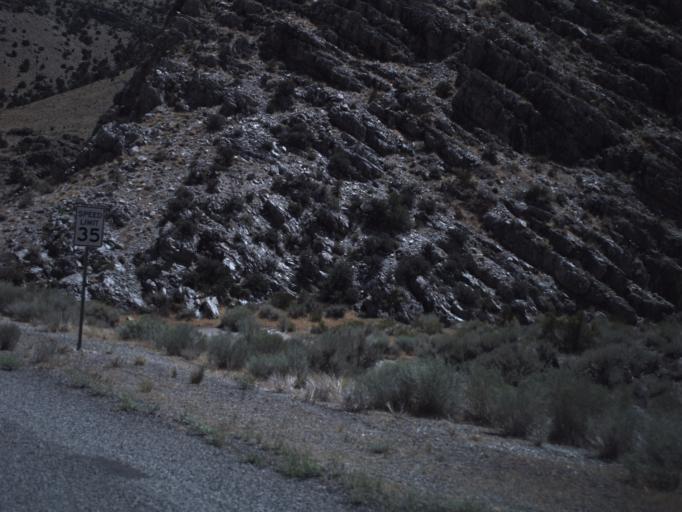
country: US
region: Utah
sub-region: Beaver County
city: Milford
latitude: 39.0843
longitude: -113.5748
